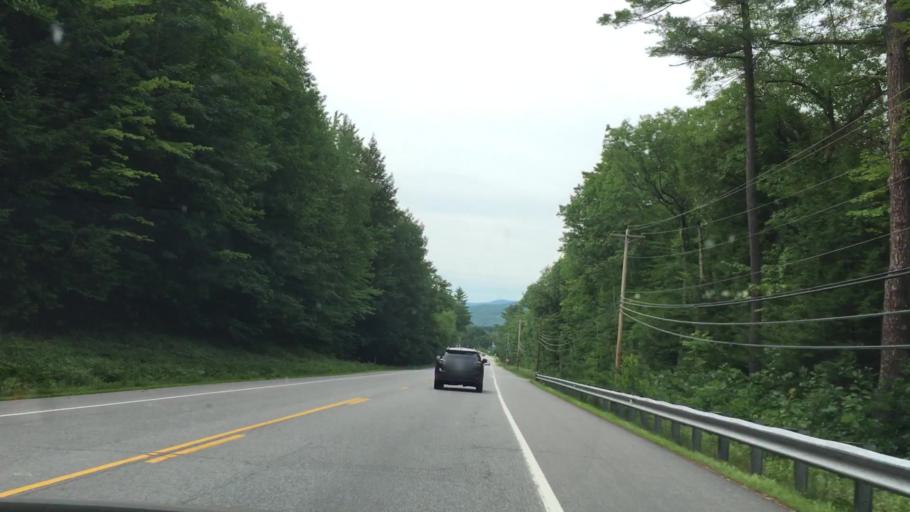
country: US
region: New Hampshire
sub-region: Carroll County
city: Center Harbor
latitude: 43.6968
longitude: -71.4597
